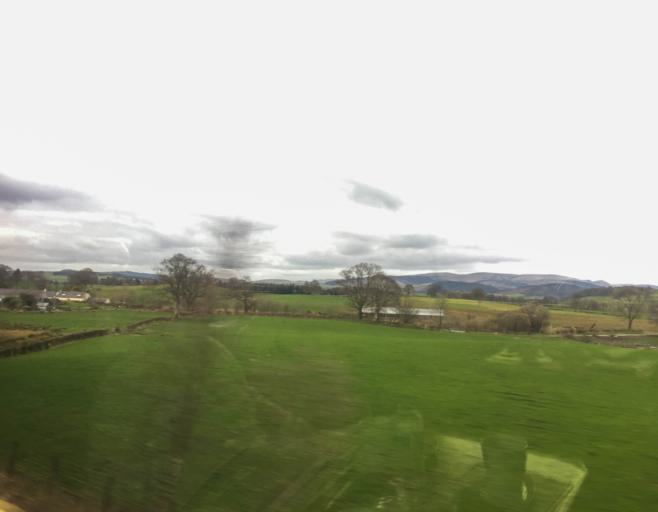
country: GB
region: Scotland
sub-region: Dumfries and Galloway
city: Moffat
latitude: 55.2894
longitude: -3.4331
